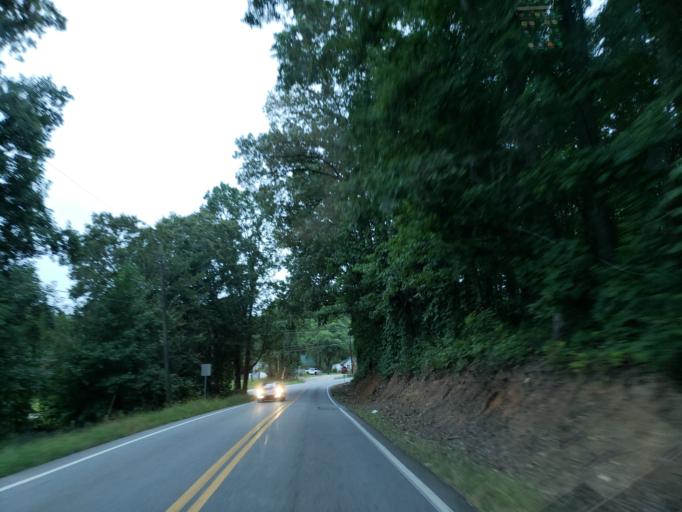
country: US
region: Georgia
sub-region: Cherokee County
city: Canton
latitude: 34.2771
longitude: -84.4497
